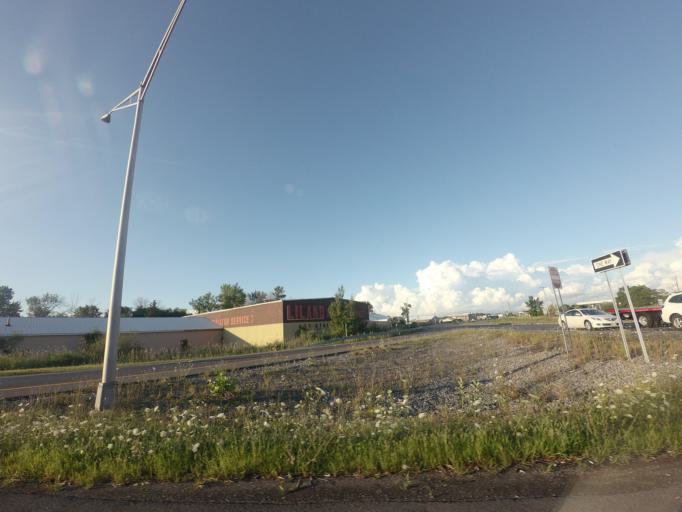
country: US
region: New York
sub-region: Onondaga County
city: East Syracuse
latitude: 43.0614
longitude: -76.0664
